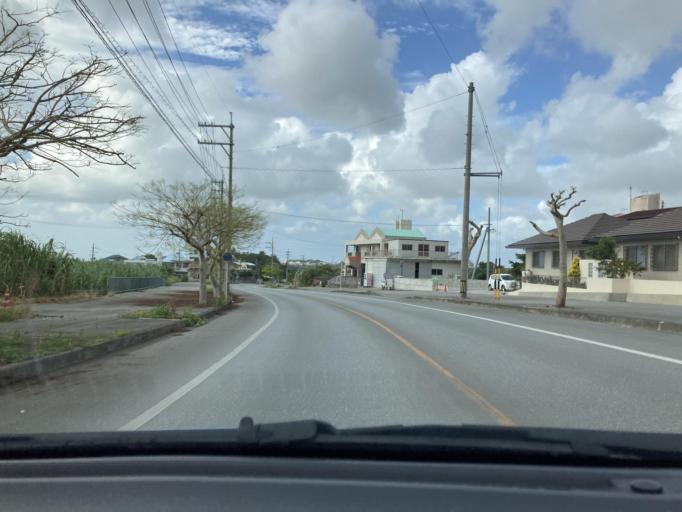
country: JP
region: Okinawa
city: Itoman
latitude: 26.1245
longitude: 127.6929
